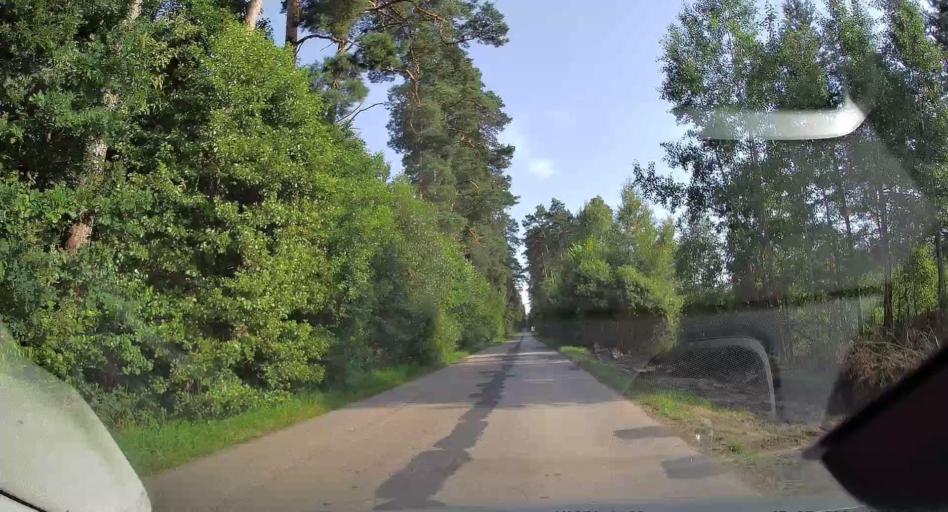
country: PL
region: Swietokrzyskie
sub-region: Powiat konecki
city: Konskie
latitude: 51.2349
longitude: 20.3818
